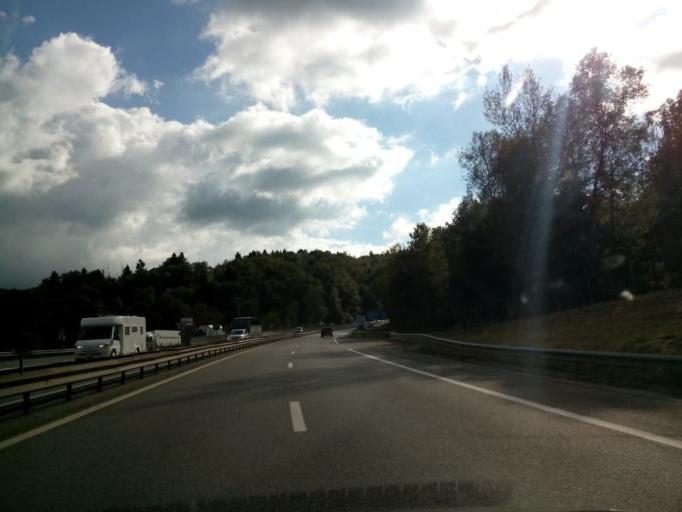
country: FR
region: Rhone-Alpes
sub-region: Departement de la Savoie
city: Novalaise
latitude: 45.5691
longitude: 5.7911
